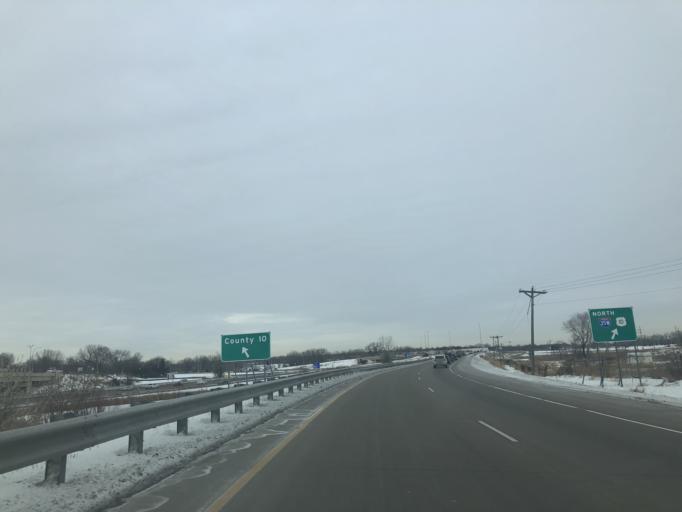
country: US
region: Minnesota
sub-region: Ramsey County
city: New Brighton
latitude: 45.0878
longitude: -93.1859
